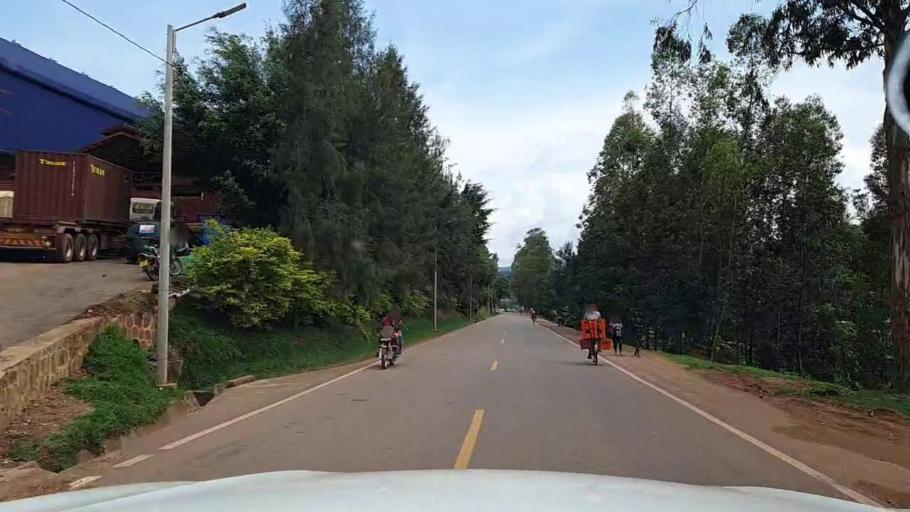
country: RW
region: Kigali
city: Kigali
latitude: -1.8700
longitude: 30.0846
